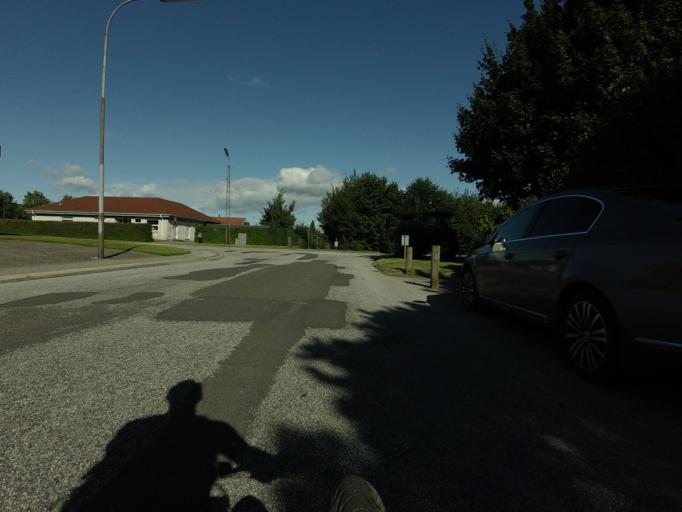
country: DK
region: Central Jutland
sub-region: Skanderborg Kommune
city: Ry
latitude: 55.9697
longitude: 9.7472
